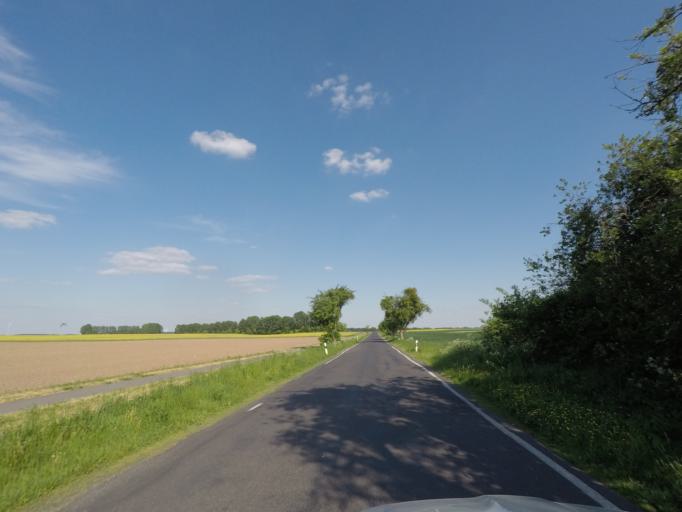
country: DE
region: Brandenburg
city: Werftpfuhl
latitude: 52.7344
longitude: 13.8513
